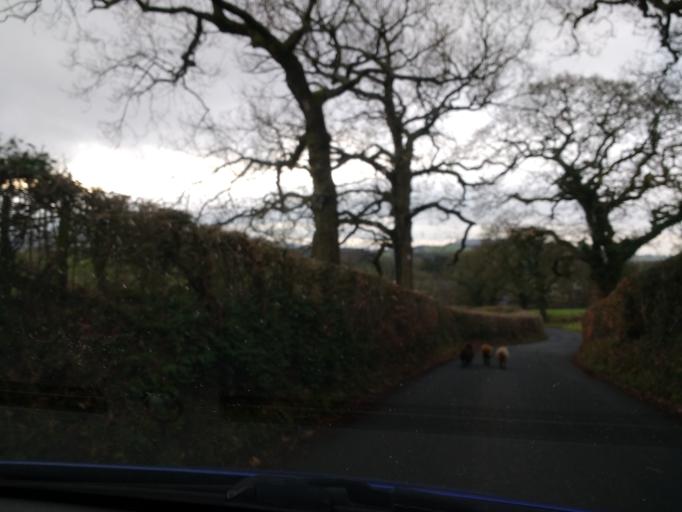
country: GB
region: England
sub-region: Lancashire
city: Caton
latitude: 54.0843
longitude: -2.7407
